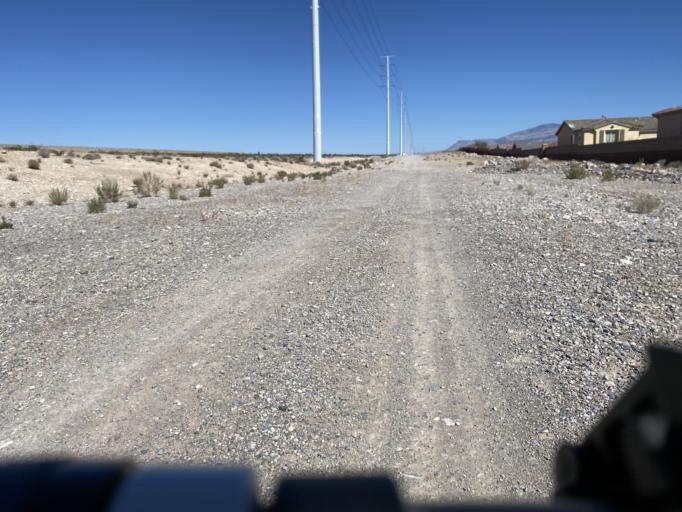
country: US
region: Nevada
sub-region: Clark County
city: Summerlin South
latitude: 36.2892
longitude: -115.3334
